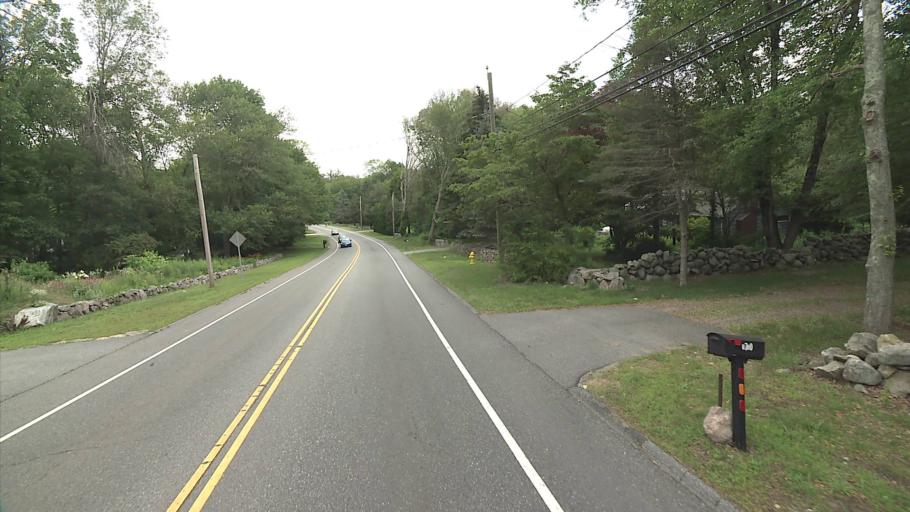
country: US
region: Connecticut
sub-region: New London County
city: Ledyard Center
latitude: 41.4073
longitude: -72.0209
